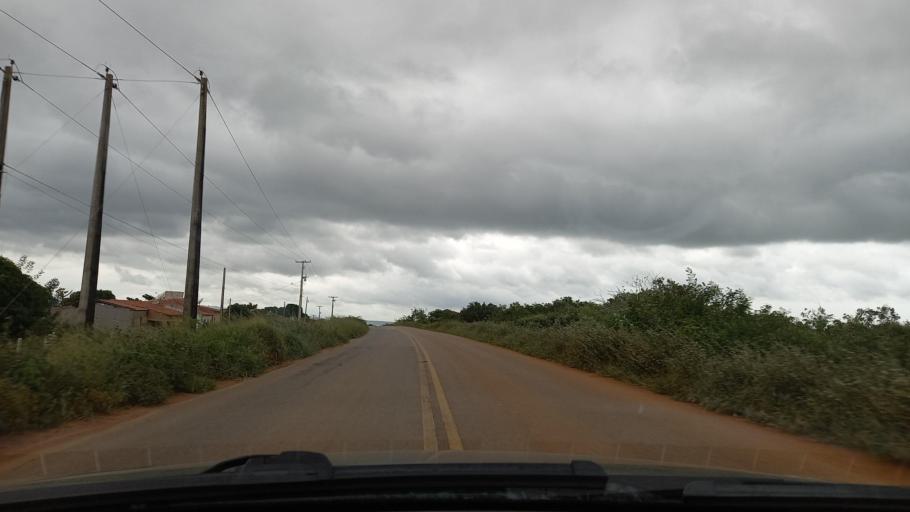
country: BR
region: Sergipe
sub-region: Caninde De Sao Francisco
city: Caninde de Sao Francisco
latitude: -9.6780
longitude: -37.8043
